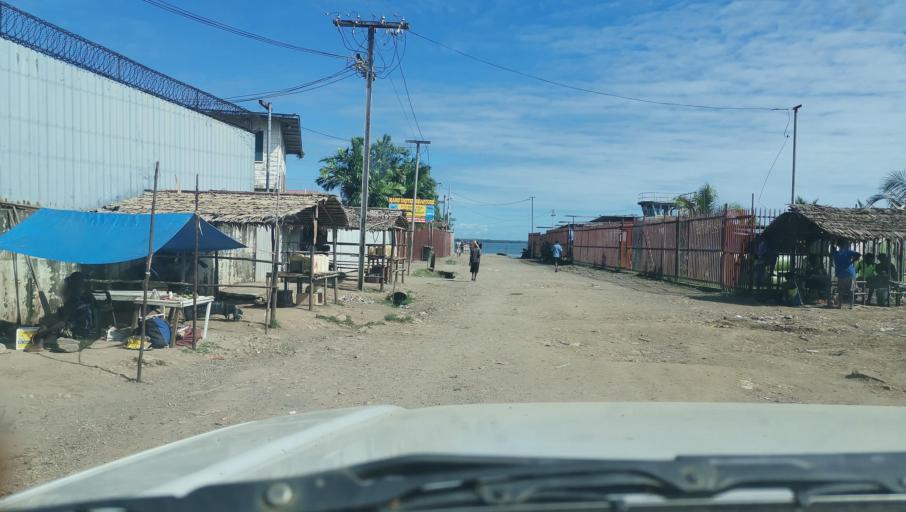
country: PG
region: Western Province
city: Daru
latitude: -9.0681
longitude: 143.2092
